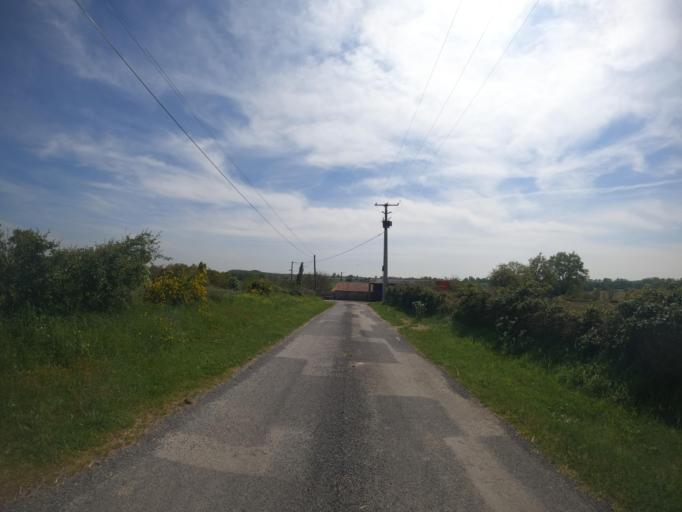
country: FR
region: Poitou-Charentes
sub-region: Departement des Deux-Sevres
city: Secondigny
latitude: 46.6445
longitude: -0.5009
